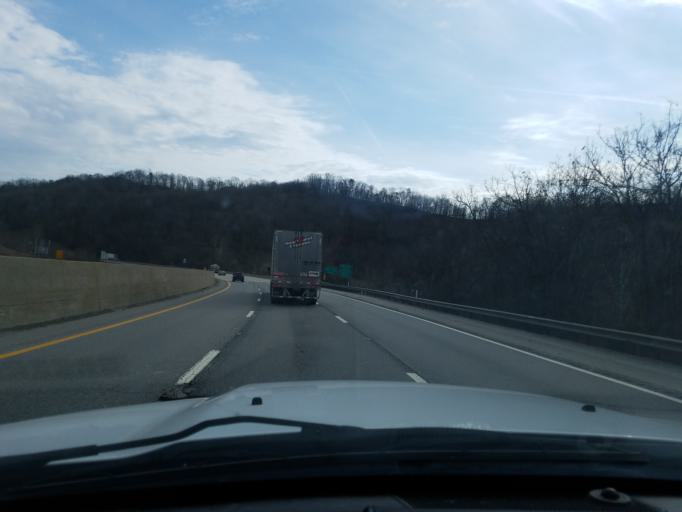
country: US
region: West Virginia
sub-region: Kanawha County
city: Nitro
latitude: 38.4308
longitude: -81.8259
